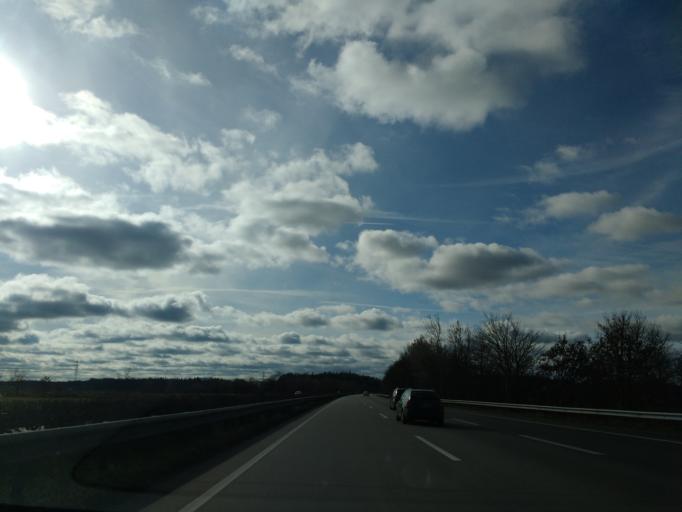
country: DE
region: Lower Saxony
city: Langen
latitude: 53.6206
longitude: 8.6644
